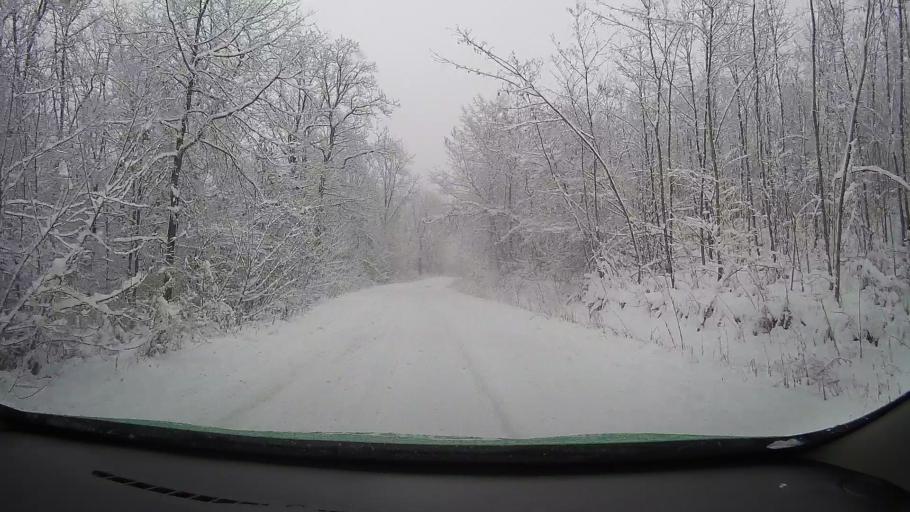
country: RO
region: Hunedoara
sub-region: Comuna Teliucu Inferior
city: Teliucu Inferior
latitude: 45.6887
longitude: 22.8997
